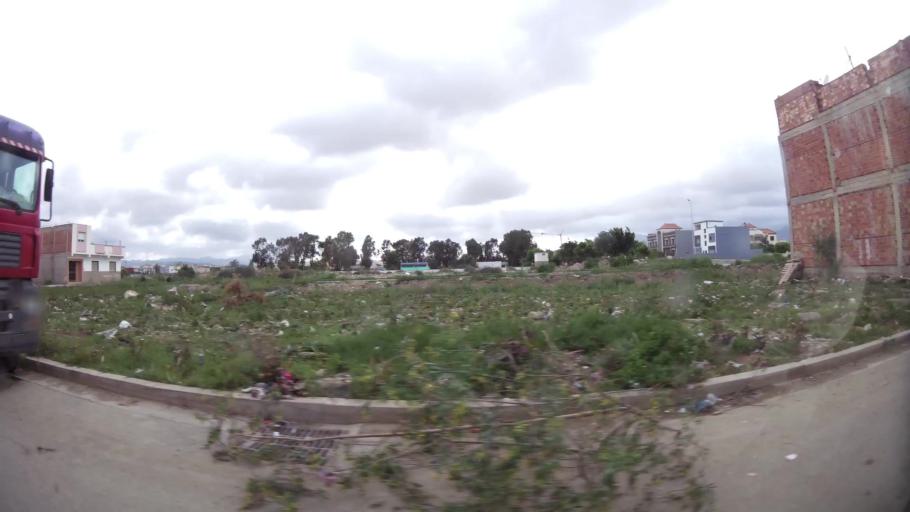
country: MA
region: Oriental
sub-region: Nador
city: Nador
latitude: 35.1611
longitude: -2.9133
